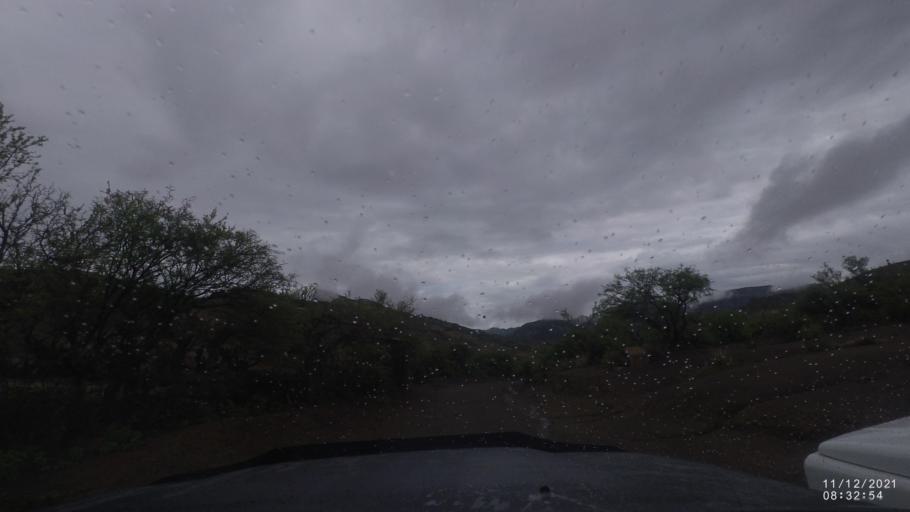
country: BO
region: Cochabamba
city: Tarata
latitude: -17.9367
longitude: -65.9332
